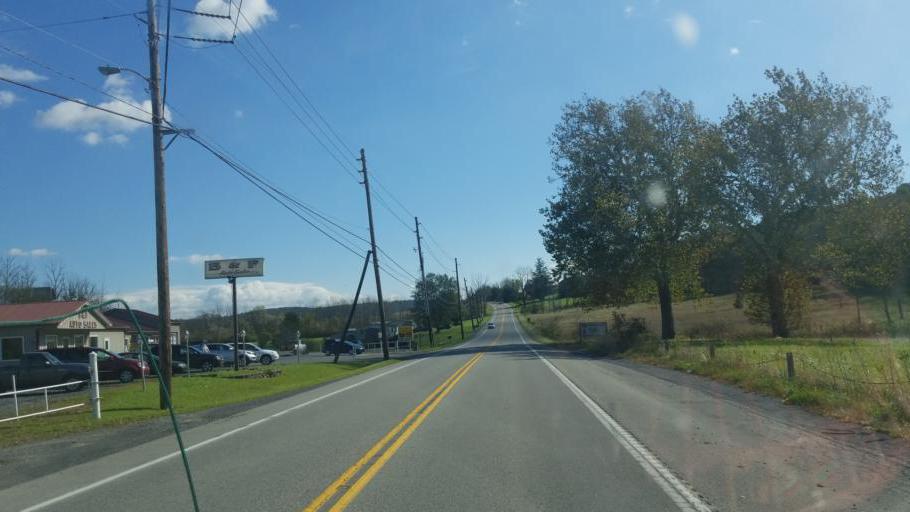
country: US
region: Pennsylvania
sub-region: Bedford County
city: Bedford
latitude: 40.0488
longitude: -78.5427
